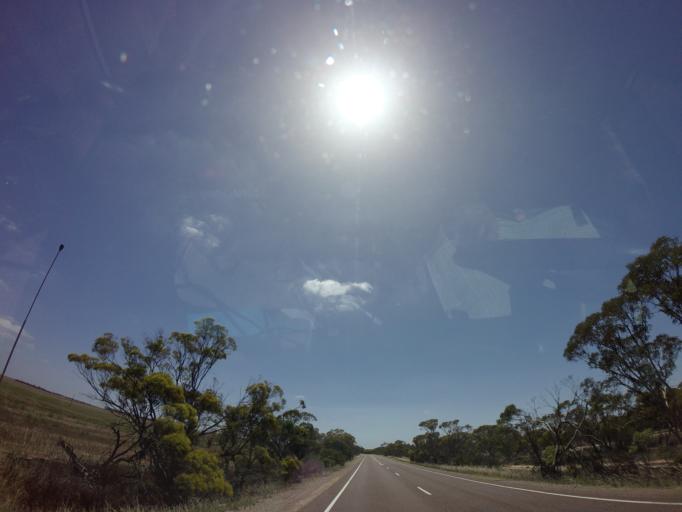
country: AU
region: South Australia
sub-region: Kimba
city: Caralue
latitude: -33.2123
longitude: 136.3545
